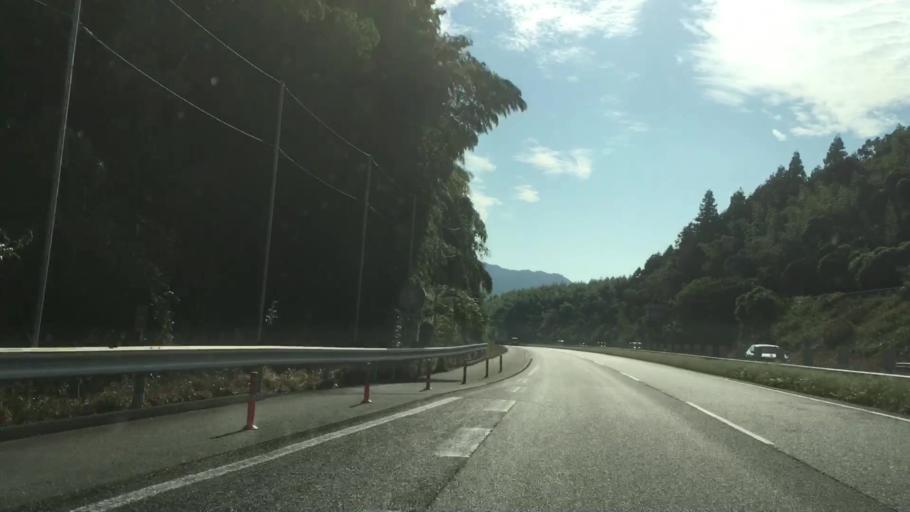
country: JP
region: Yamaguchi
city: Hikari
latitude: 34.0342
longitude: 131.9701
